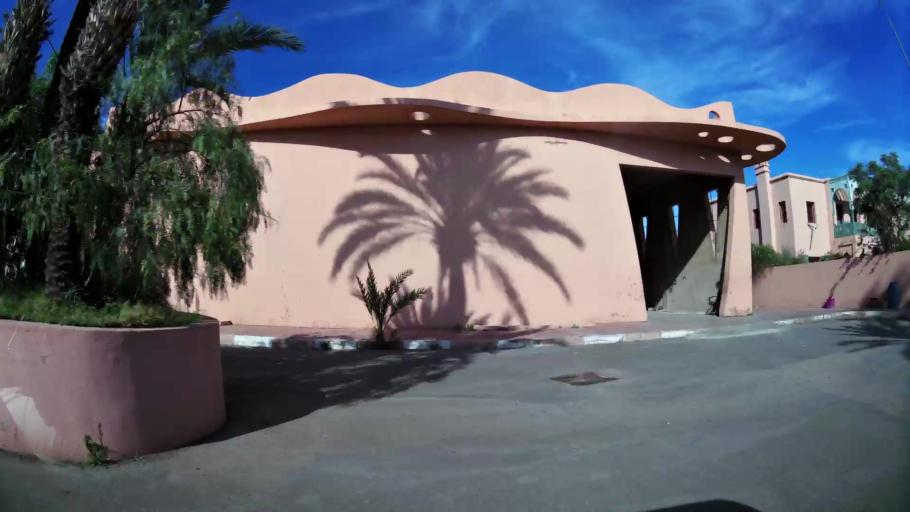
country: MA
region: Marrakech-Tensift-Al Haouz
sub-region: Marrakech
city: Marrakesh
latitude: 31.6777
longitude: -8.0555
